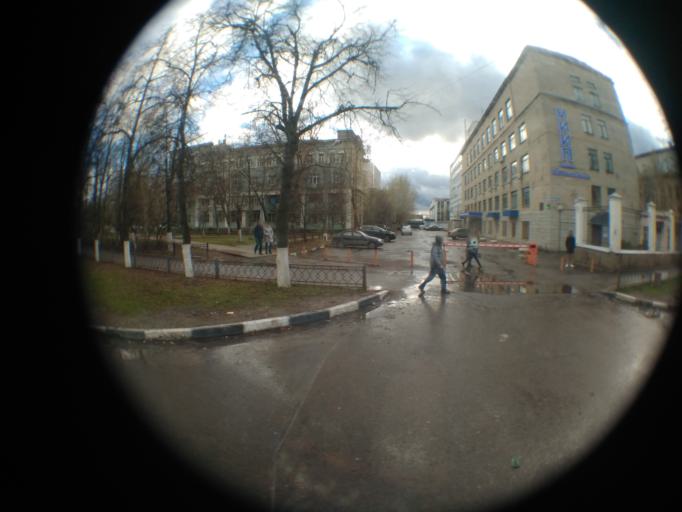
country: RU
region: Moskovskaya
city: Zhukovskiy
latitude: 55.5980
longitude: 38.1123
